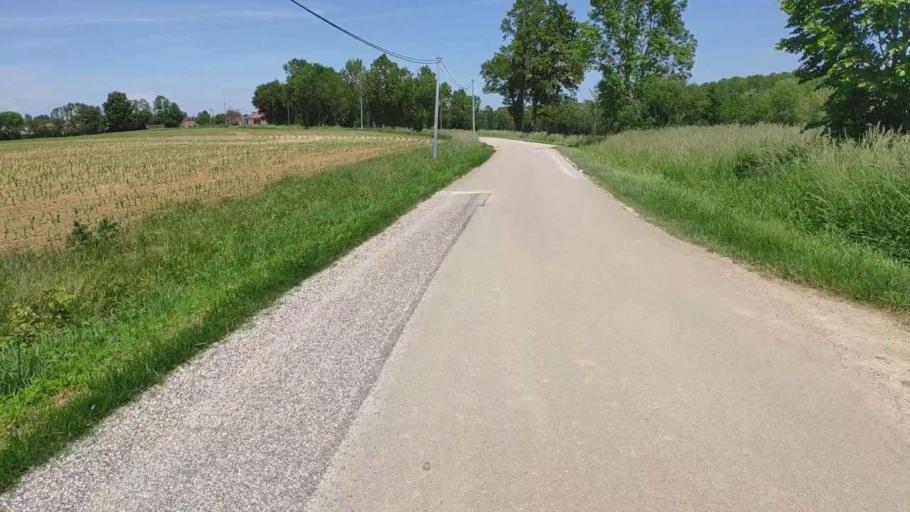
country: FR
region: Franche-Comte
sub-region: Departement du Jura
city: Bletterans
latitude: 46.7951
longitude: 5.3779
